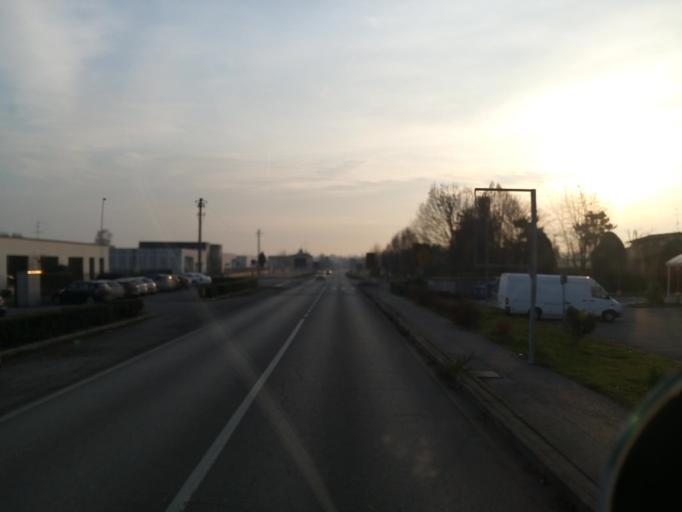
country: IT
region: Lombardy
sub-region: Provincia di Brescia
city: Flero
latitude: 45.4719
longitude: 10.1768
